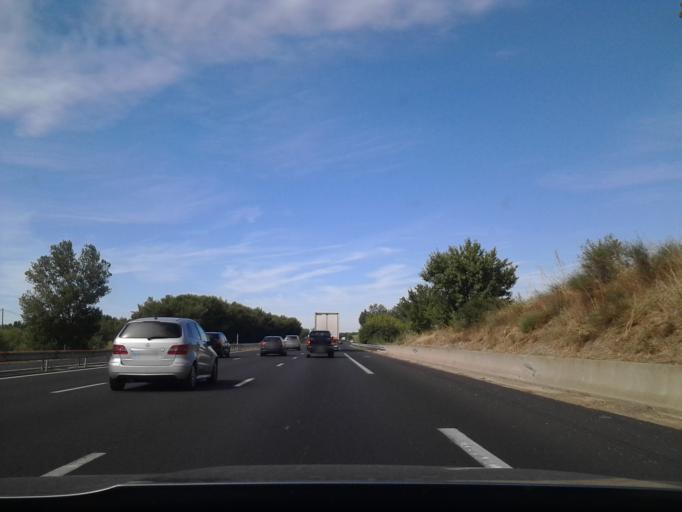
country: FR
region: Languedoc-Roussillon
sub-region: Departement de l'Herault
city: Pinet
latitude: 43.4263
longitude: 3.5557
